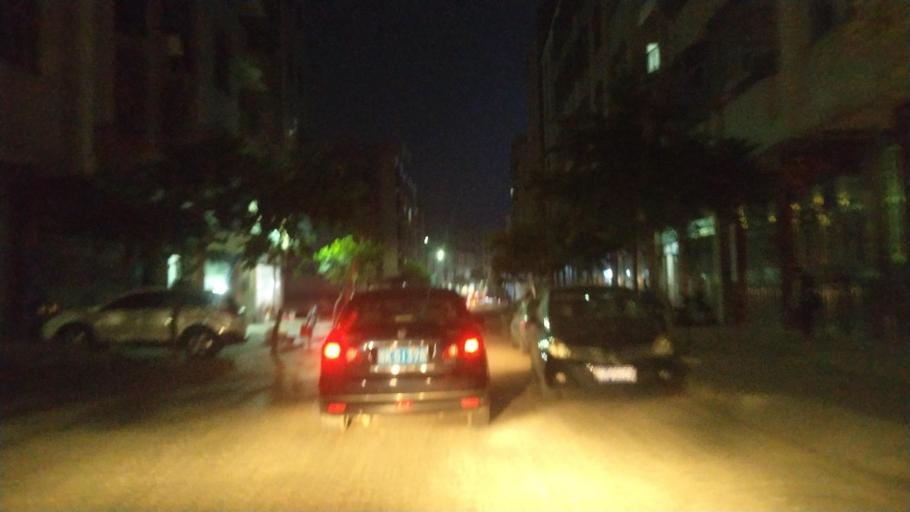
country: CN
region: Guangdong
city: Xiaguo
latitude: 21.6481
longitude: 110.6310
